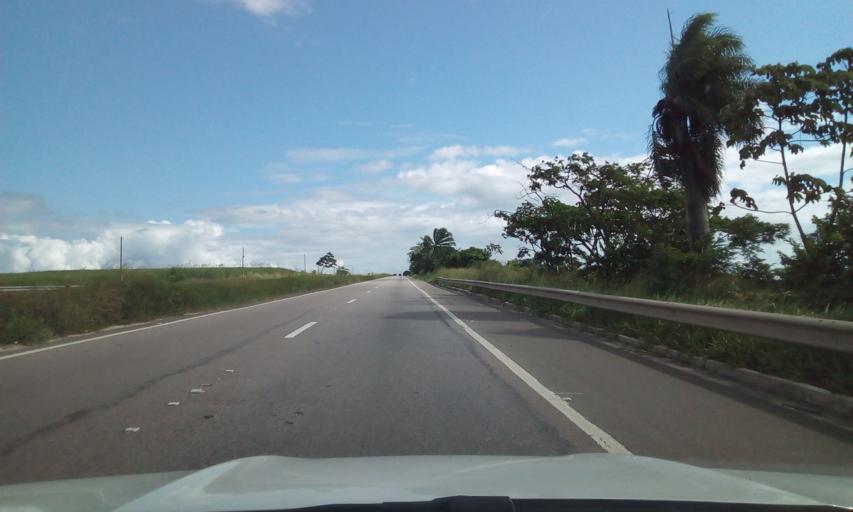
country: BR
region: Pernambuco
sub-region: Itapissuma
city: Itapissuma
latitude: -7.7089
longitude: -34.9288
